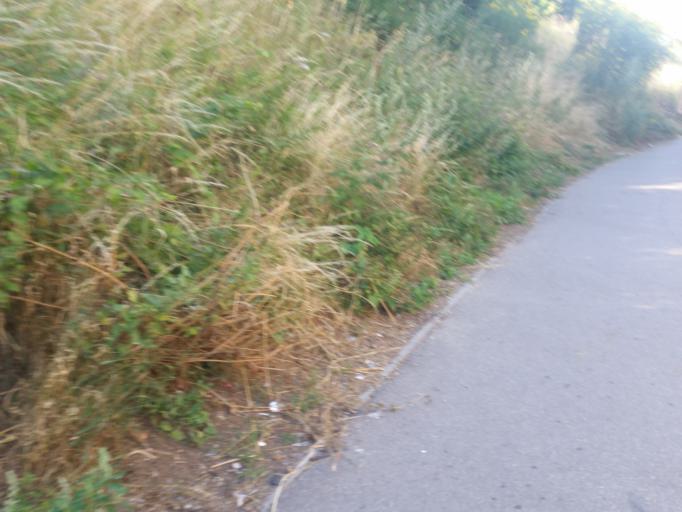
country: GB
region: England
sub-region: Greater London
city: Harringay
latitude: 51.5655
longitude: -0.1057
